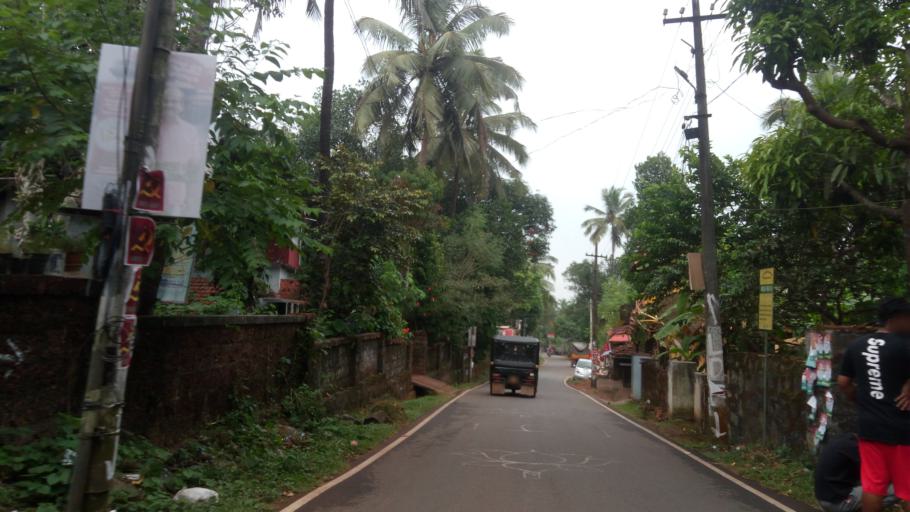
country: IN
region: Kerala
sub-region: Malappuram
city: Malappuram
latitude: 10.9891
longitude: 76.0074
